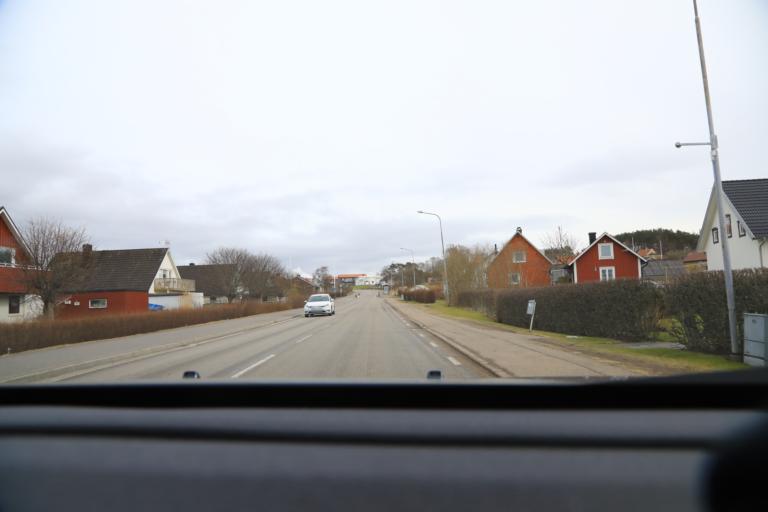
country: SE
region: Halland
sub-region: Kungsbacka Kommun
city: Frillesas
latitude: 57.2382
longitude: 12.1172
